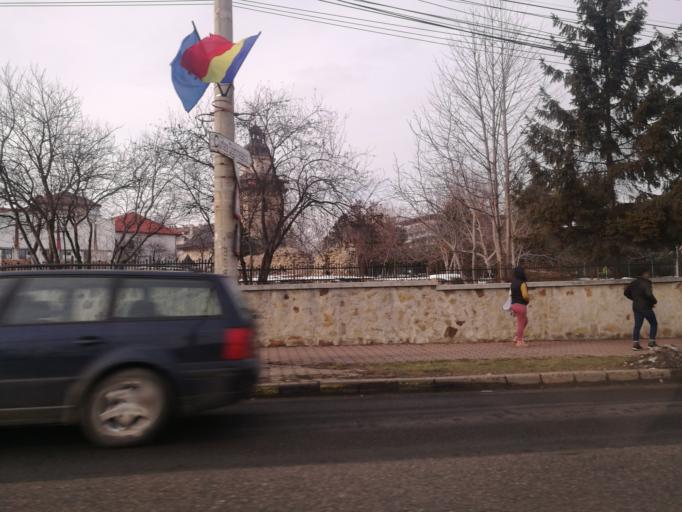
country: RO
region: Suceava
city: Suceava
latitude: 47.6453
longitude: 26.2634
